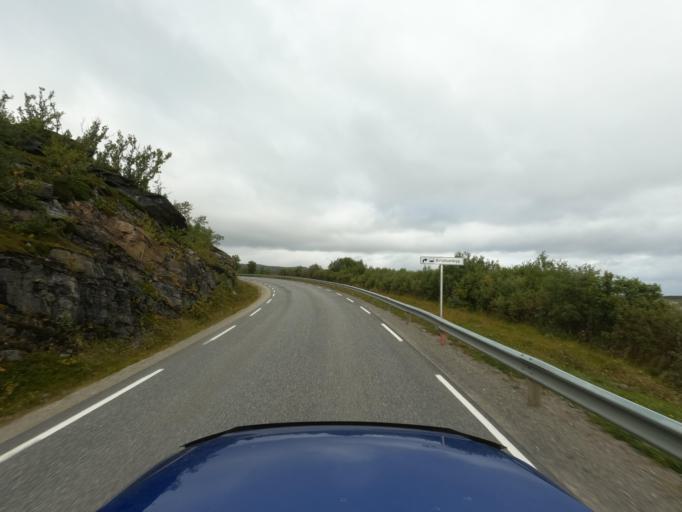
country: NO
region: Finnmark Fylke
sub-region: Porsanger
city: Lakselv
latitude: 70.3424
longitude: 25.0776
